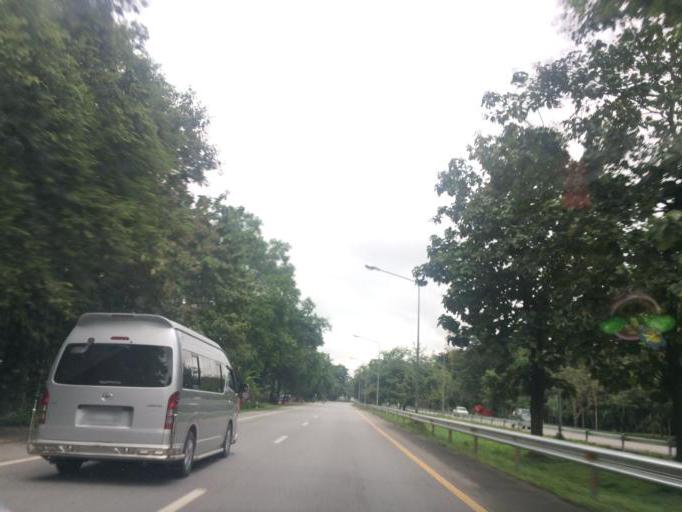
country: TH
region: Chiang Rai
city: Chiang Rai
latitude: 19.8347
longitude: 99.7848
